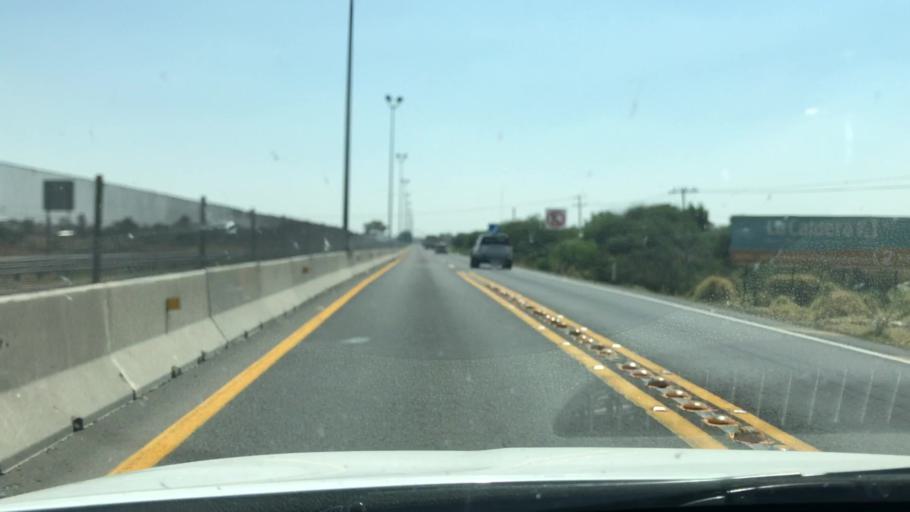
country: MX
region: Guanajuato
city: Abasolo
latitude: 20.4552
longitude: -101.5408
